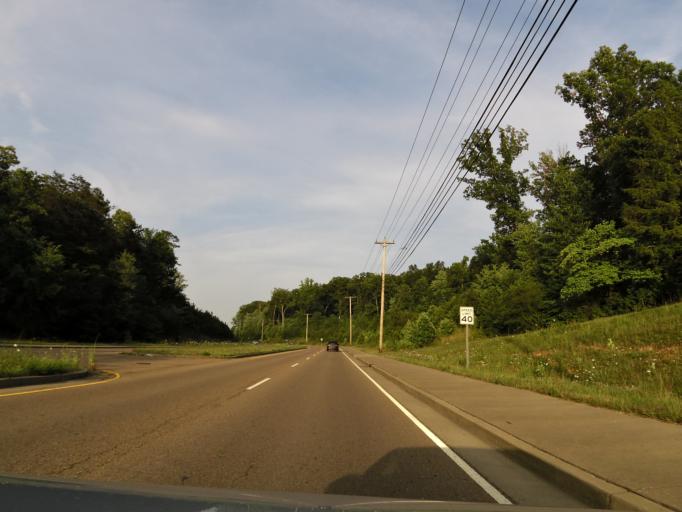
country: US
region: Tennessee
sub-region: Knox County
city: Farragut
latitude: 35.9453
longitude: -84.1096
